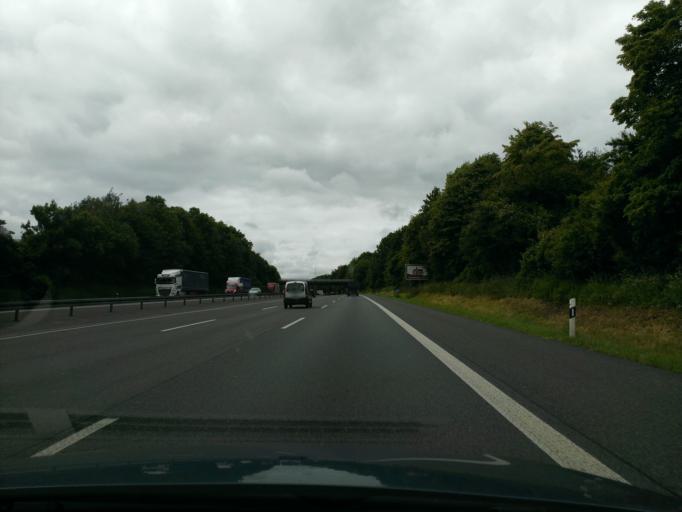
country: DE
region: North Rhine-Westphalia
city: Burscheid
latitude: 51.1110
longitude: 7.1453
